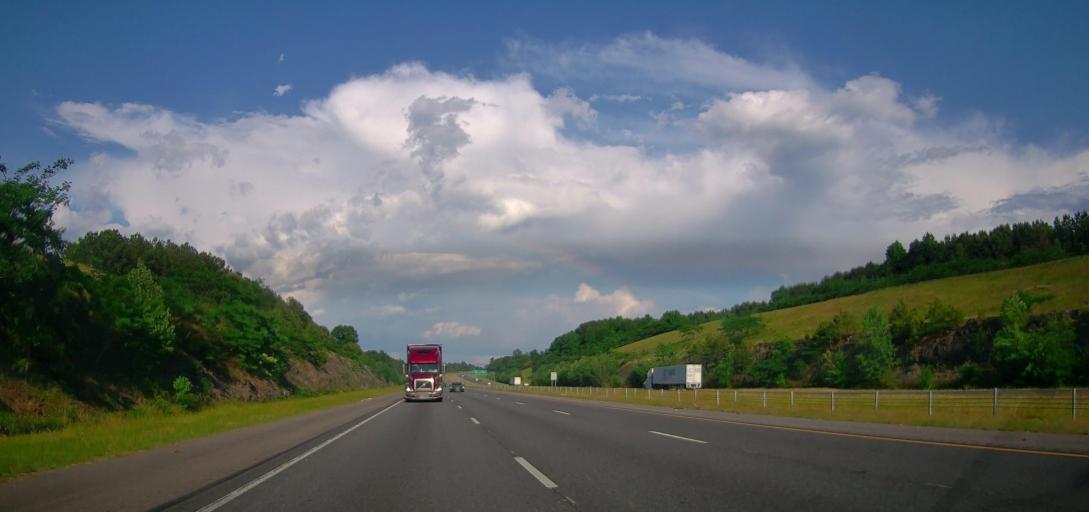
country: US
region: Alabama
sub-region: Jefferson County
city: Fultondale
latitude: 33.5881
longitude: -86.8447
